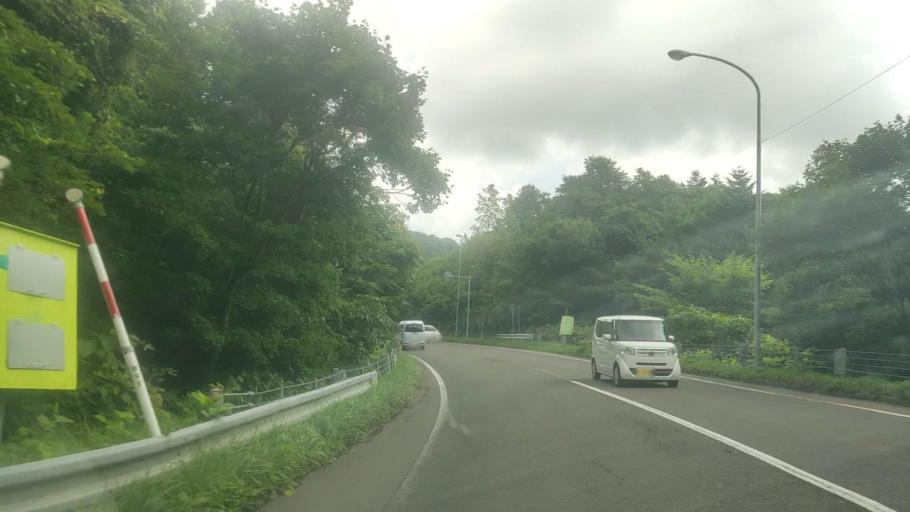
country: JP
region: Hokkaido
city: Niseko Town
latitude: 42.5973
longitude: 140.4627
